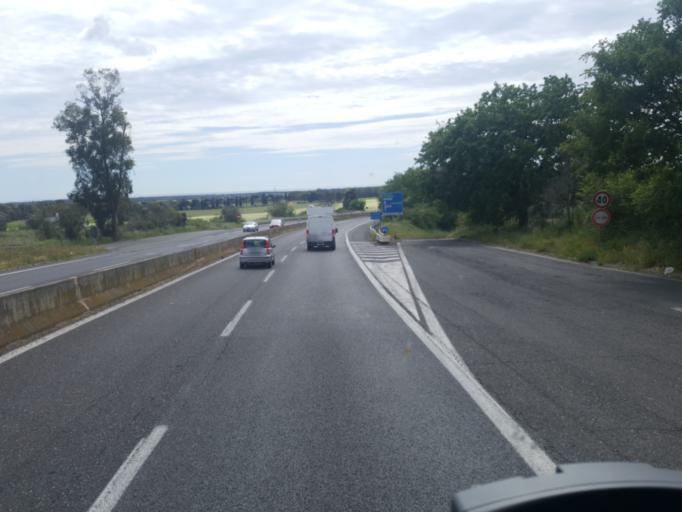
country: IT
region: Latium
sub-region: Citta metropolitana di Roma Capitale
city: Ara Nova
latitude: 41.9154
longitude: 12.2257
